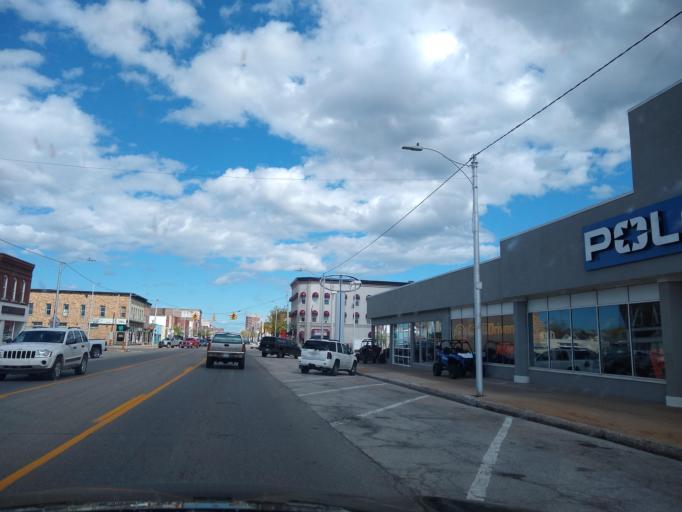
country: US
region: Michigan
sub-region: Delta County
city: Escanaba
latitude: 45.7457
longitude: -87.0683
